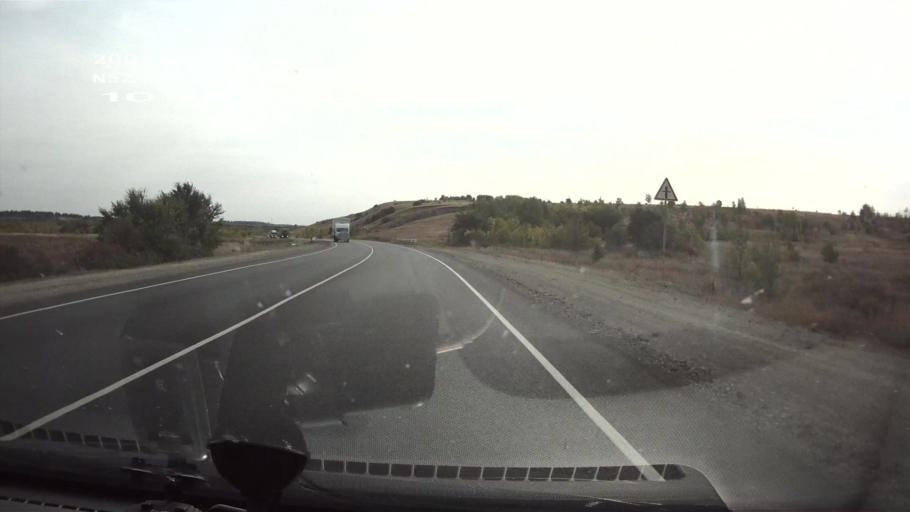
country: RU
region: Saratov
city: Sennoy
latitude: 52.1010
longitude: 46.8151
